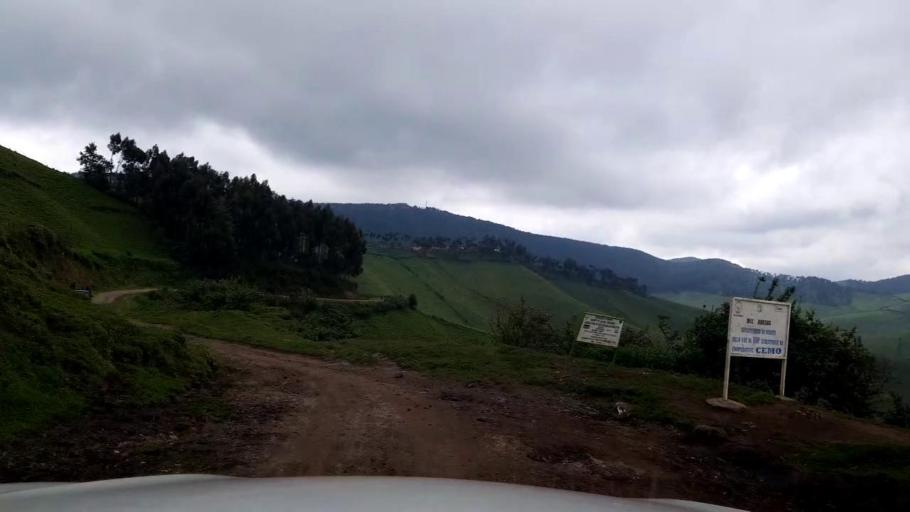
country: RW
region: Western Province
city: Gisenyi
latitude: -1.6771
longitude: 29.4129
